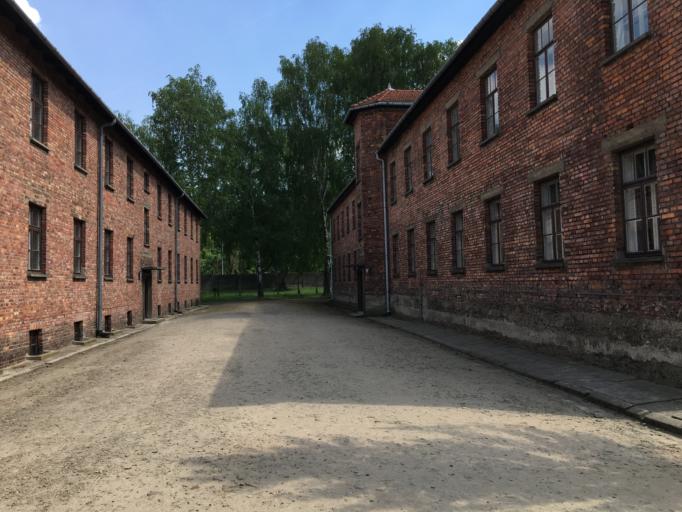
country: PL
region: Lesser Poland Voivodeship
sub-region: Powiat oswiecimski
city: Oswiecim
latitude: 50.0259
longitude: 19.2039
